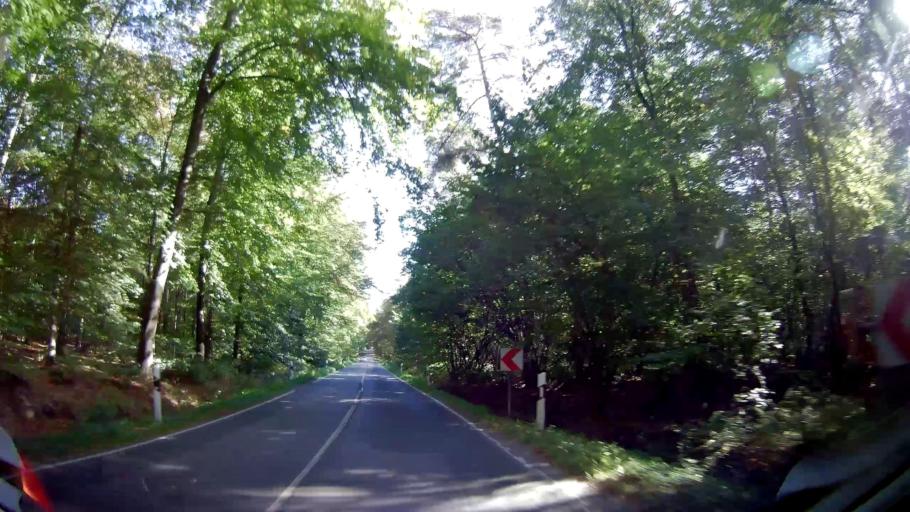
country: DE
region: North Rhine-Westphalia
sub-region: Regierungsbezirk Dusseldorf
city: Hunxe
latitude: 51.6039
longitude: 6.8191
